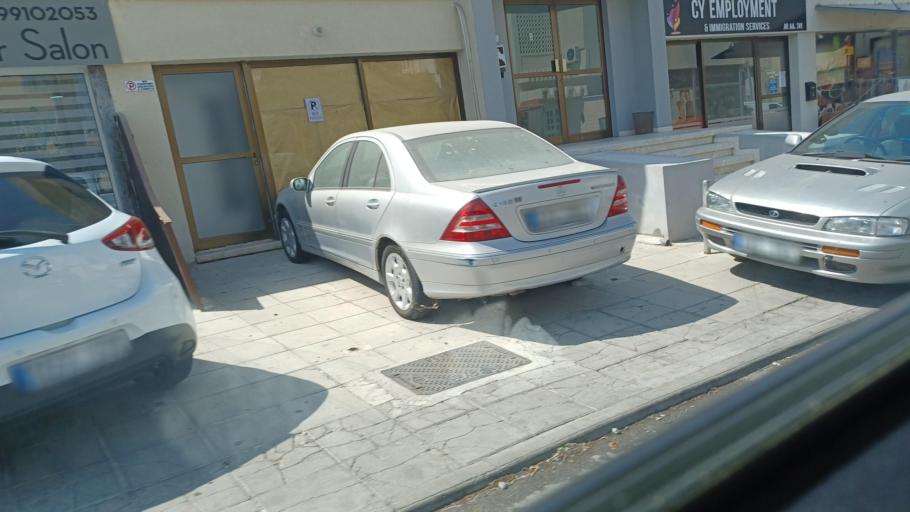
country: CY
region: Pafos
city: Paphos
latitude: 34.7816
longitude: 32.4279
